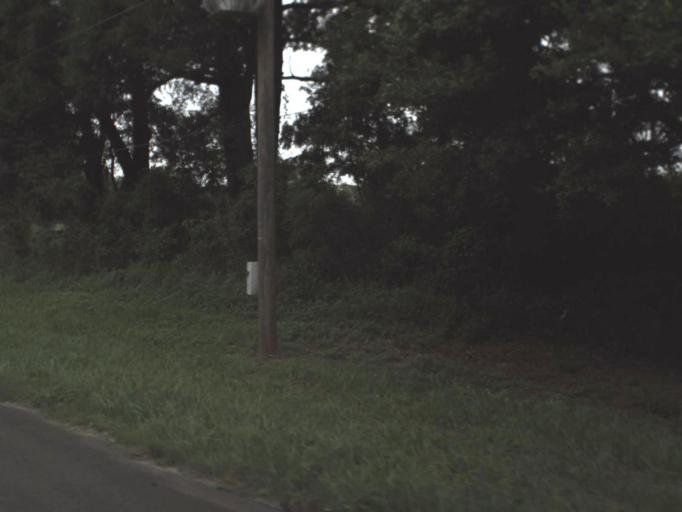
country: US
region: Florida
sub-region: Alachua County
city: Archer
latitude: 29.5025
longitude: -82.4982
